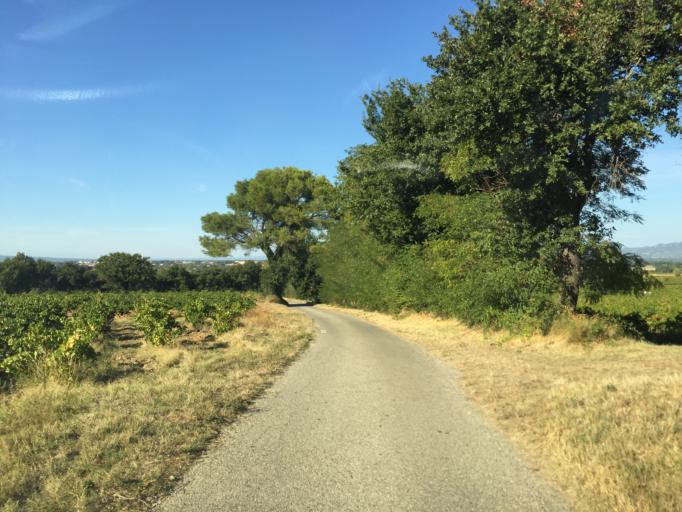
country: FR
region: Provence-Alpes-Cote d'Azur
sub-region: Departement du Vaucluse
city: Courthezon
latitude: 44.0624
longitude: 4.8776
